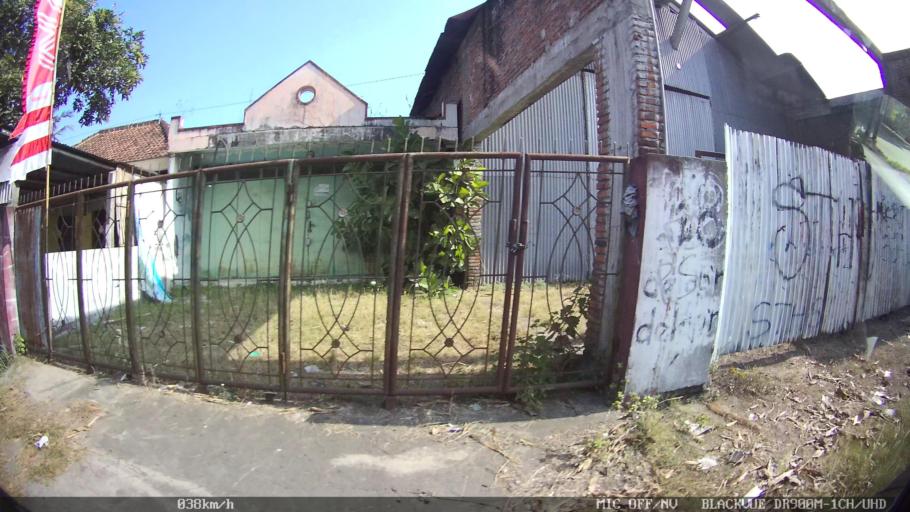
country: ID
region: Daerah Istimewa Yogyakarta
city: Sewon
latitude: -7.8720
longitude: 110.3646
